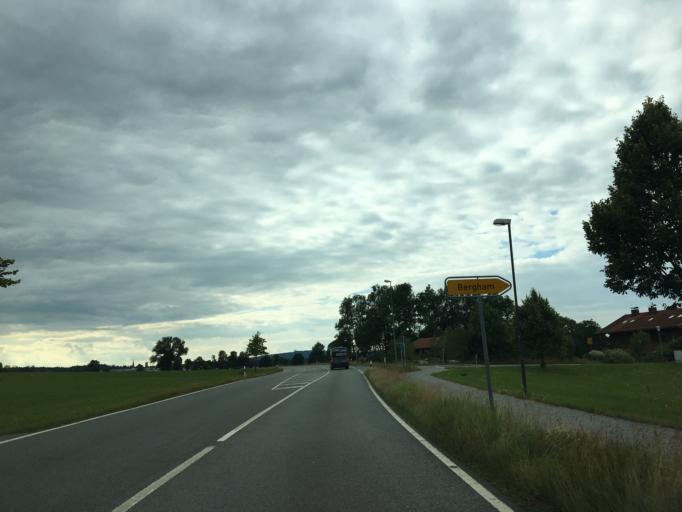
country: DE
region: Bavaria
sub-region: Upper Bavaria
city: Miesbach
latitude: 47.7875
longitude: 11.8545
